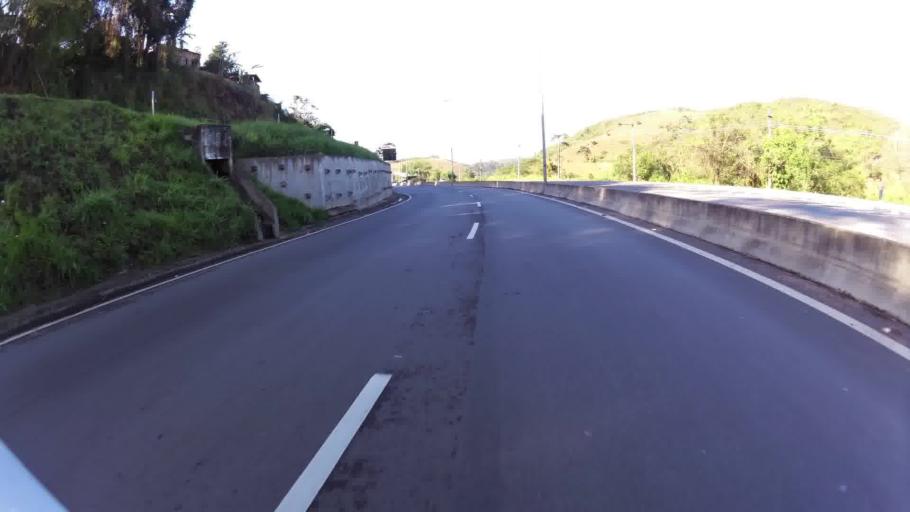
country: BR
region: Rio de Janeiro
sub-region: Petropolis
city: Petropolis
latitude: -22.6130
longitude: -43.2866
